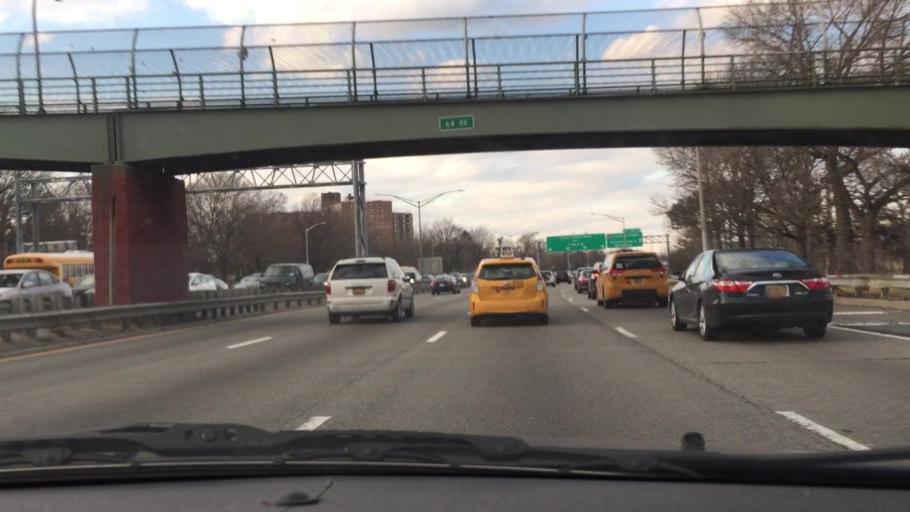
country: US
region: New York
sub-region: Queens County
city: Borough of Queens
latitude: 40.7340
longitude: -73.8440
